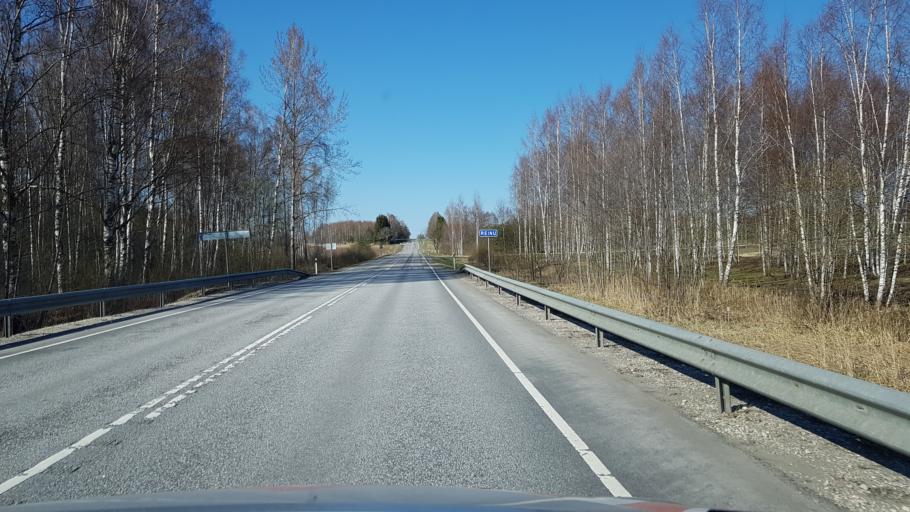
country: EE
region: Jogevamaa
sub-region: Tabivere vald
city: Tabivere
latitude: 58.5530
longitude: 26.7535
